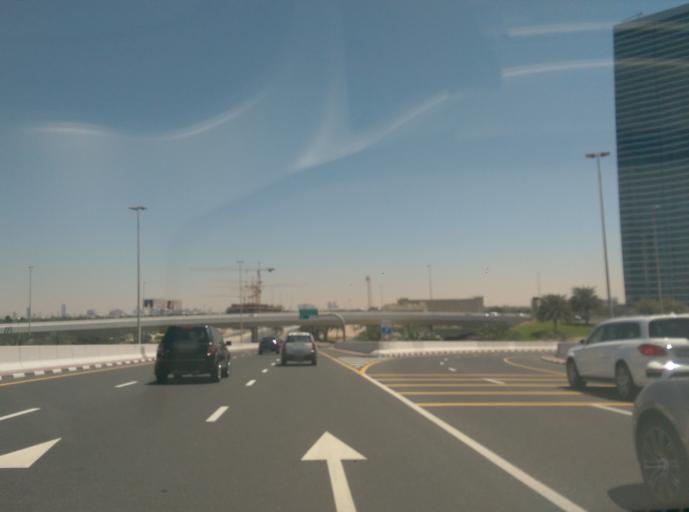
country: AE
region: Dubai
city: Dubai
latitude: 25.0838
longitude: 55.1523
